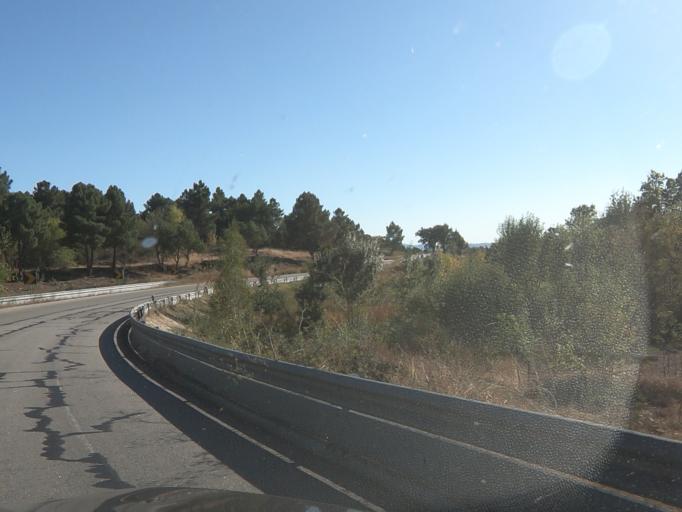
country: PT
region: Vila Real
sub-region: Valpacos
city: Valpacos
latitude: 41.6400
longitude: -7.3161
